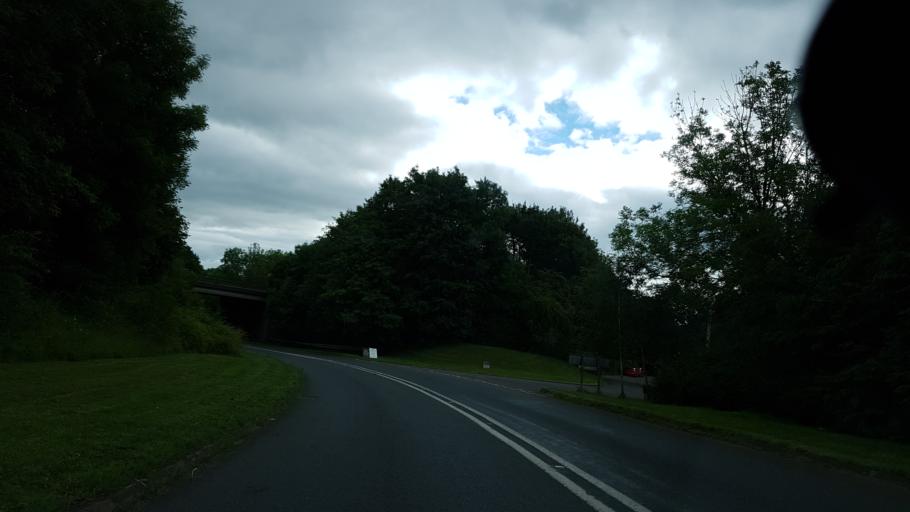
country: GB
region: Wales
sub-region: Monmouthshire
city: Llanarth
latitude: 51.7725
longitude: -2.8740
